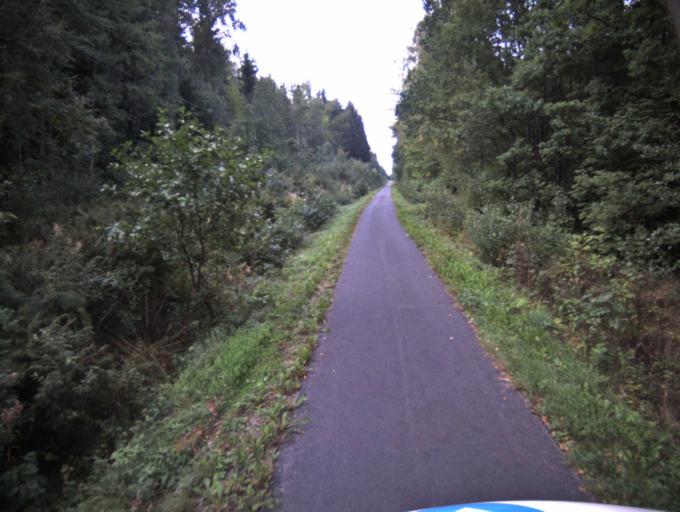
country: SE
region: Vaestra Goetaland
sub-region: Ulricehamns Kommun
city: Ulricehamn
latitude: 57.6961
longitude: 13.3919
